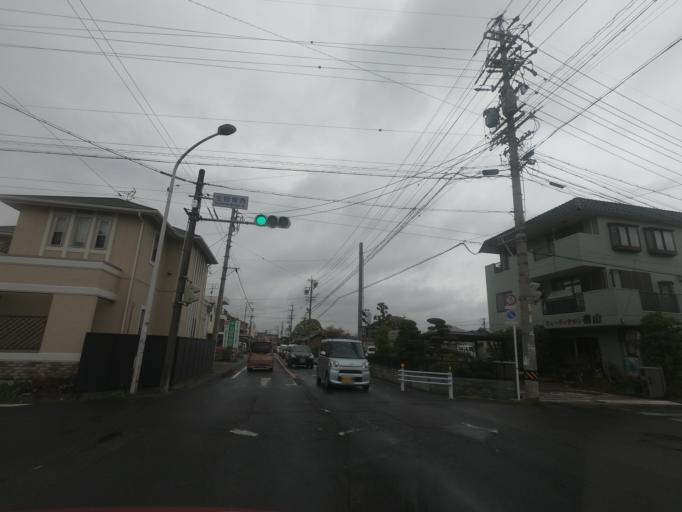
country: JP
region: Aichi
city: Kasugai
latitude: 35.2485
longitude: 136.9926
